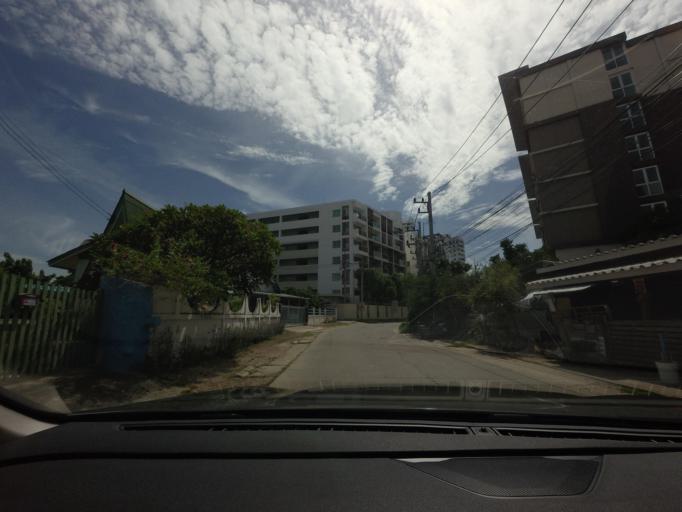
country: TH
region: Prachuap Khiri Khan
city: Hua Hin
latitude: 12.5149
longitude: 99.9750
